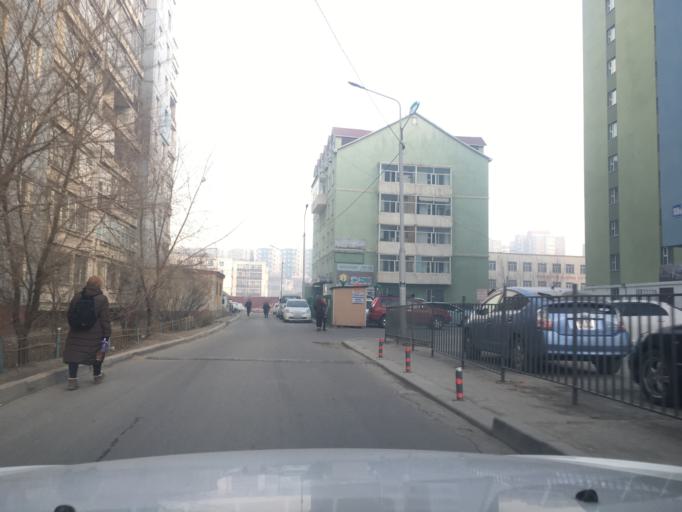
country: MN
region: Ulaanbaatar
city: Ulaanbaatar
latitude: 47.9149
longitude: 106.8656
